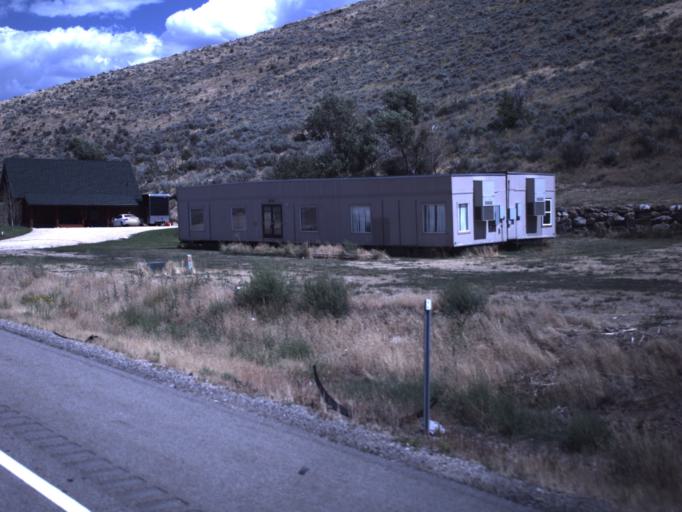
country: US
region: Utah
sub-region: Wasatch County
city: Midway
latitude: 40.4573
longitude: -111.4693
